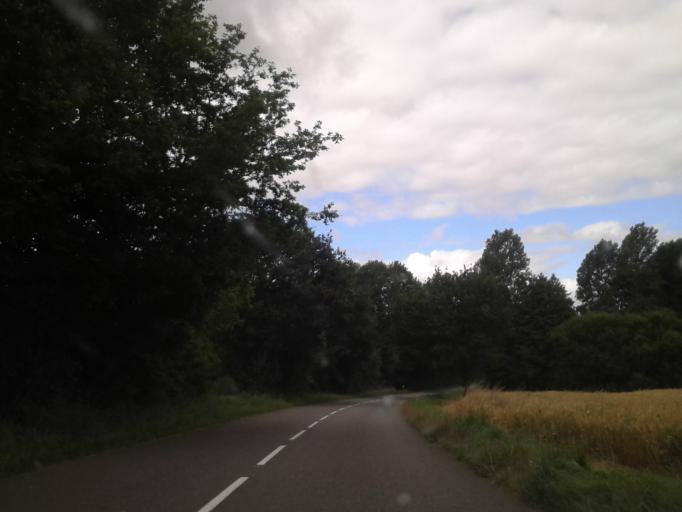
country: FR
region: Pays de la Loire
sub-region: Departement de la Mayenne
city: Gorron
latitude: 48.4658
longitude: -0.7347
